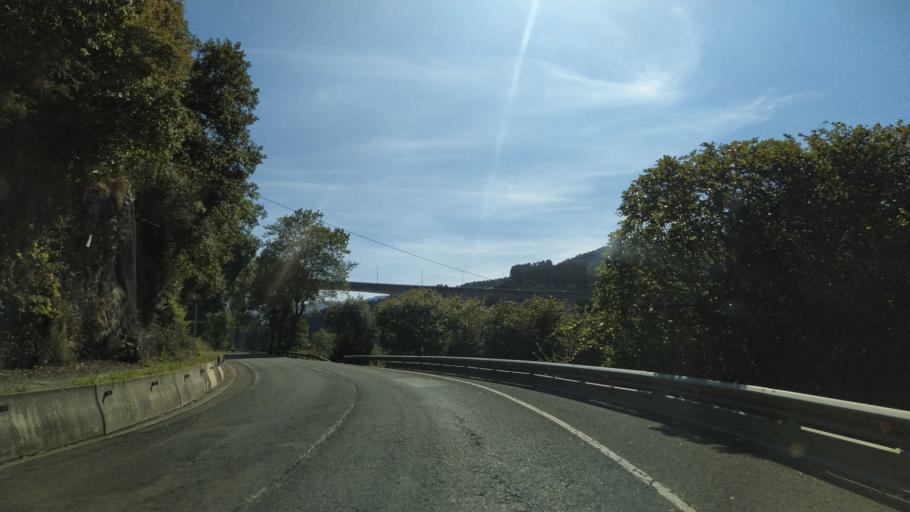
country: ES
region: Cantabria
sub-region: Provincia de Cantabria
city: Liendo
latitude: 43.3884
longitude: -3.3185
